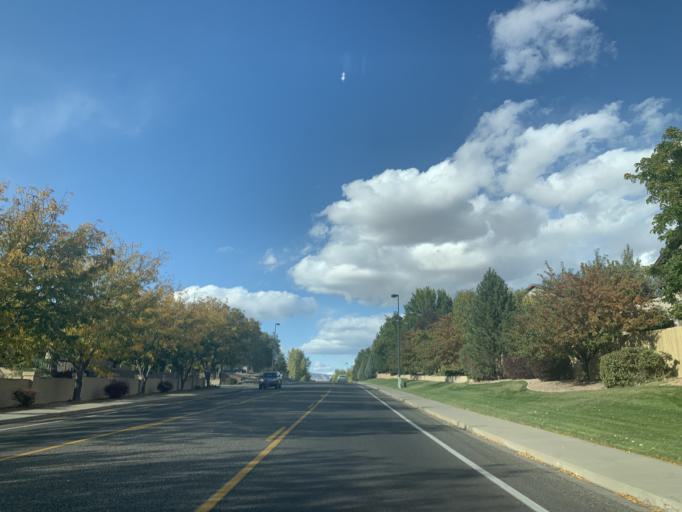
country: US
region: Colorado
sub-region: Mesa County
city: Grand Junction
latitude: 39.0971
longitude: -108.5430
